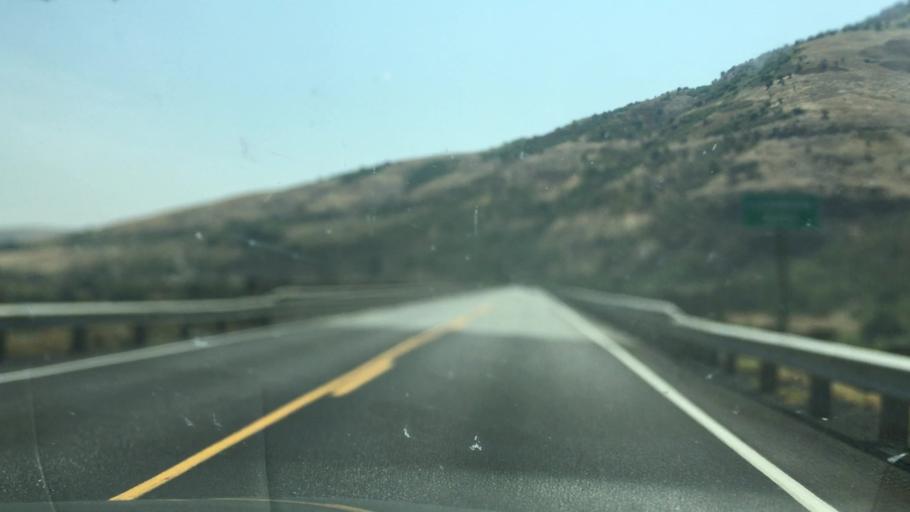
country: US
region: Idaho
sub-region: Nez Perce County
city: Lapwai
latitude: 46.4440
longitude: -116.8479
